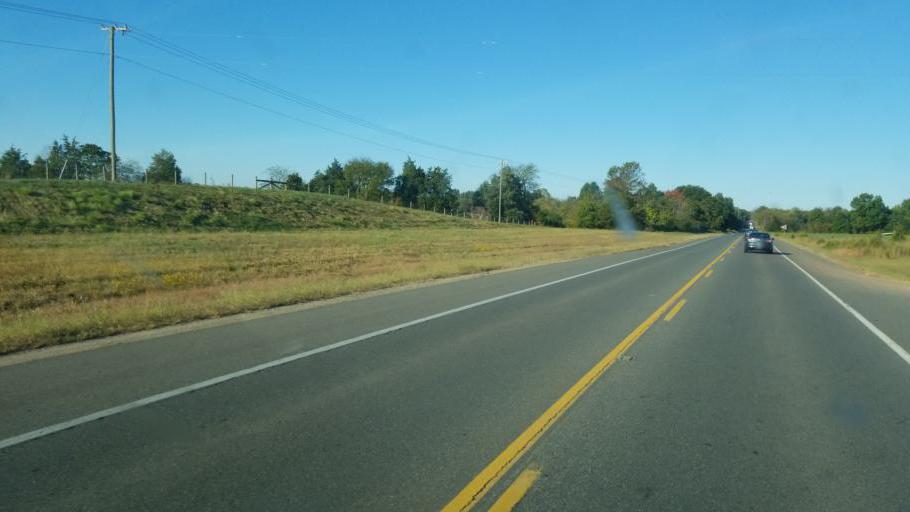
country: US
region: Virginia
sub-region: Fauquier County
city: Bealeton
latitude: 38.5989
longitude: -77.7305
